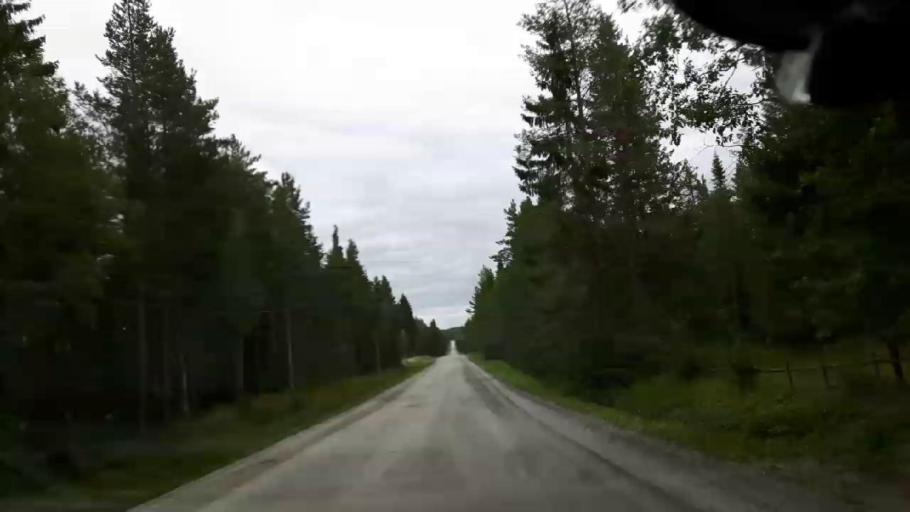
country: SE
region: Jaemtland
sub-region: OEstersunds Kommun
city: Brunflo
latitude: 63.1010
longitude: 15.1107
